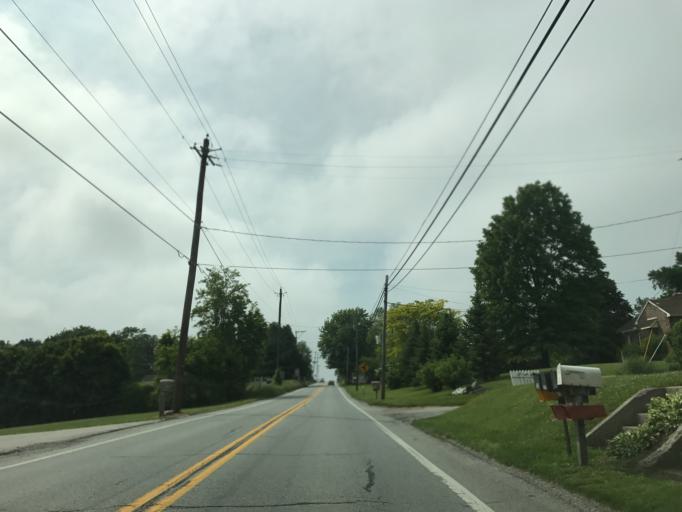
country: US
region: Pennsylvania
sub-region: York County
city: Windsor
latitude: 39.8963
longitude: -76.5667
